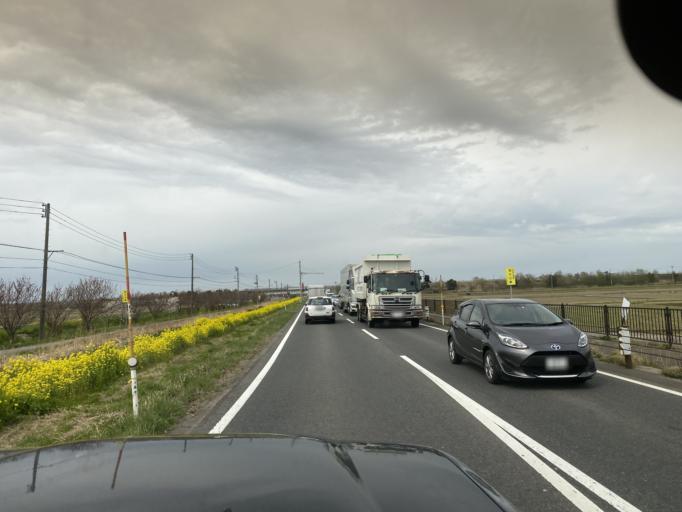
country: JP
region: Niigata
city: Niitsu-honcho
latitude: 37.8166
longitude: 139.0998
